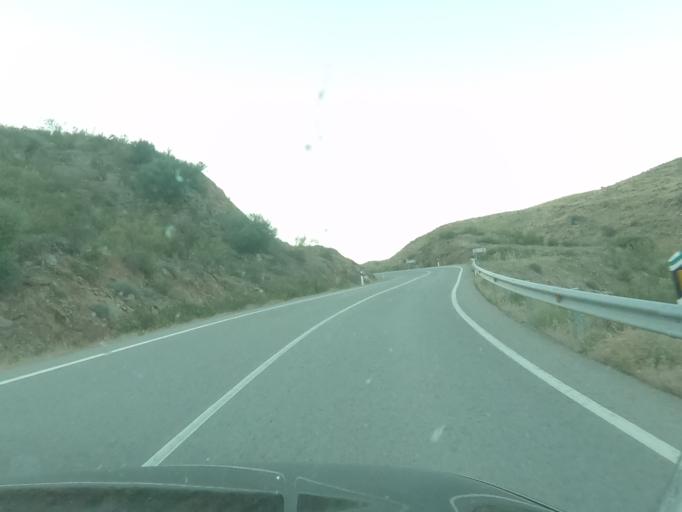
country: ES
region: Extremadura
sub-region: Provincia de Caceres
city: Salorino
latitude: 39.5777
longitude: -6.9972
